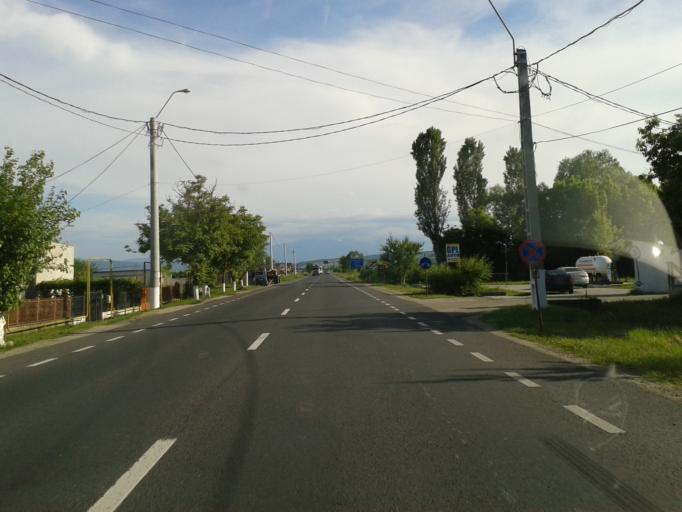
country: RO
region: Hunedoara
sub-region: Comuna Calan
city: Calan
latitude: 45.7312
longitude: 22.9964
